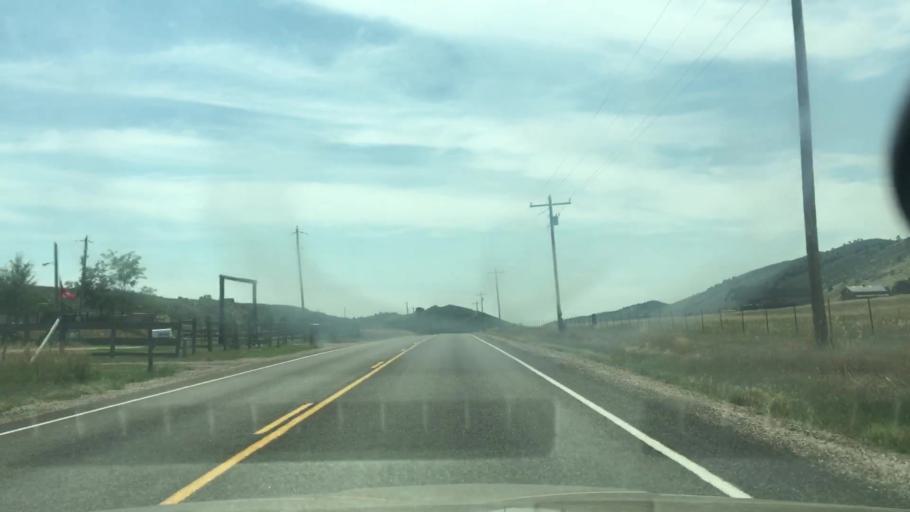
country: US
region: Colorado
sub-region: Larimer County
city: Campion
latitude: 40.3499
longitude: -105.1836
